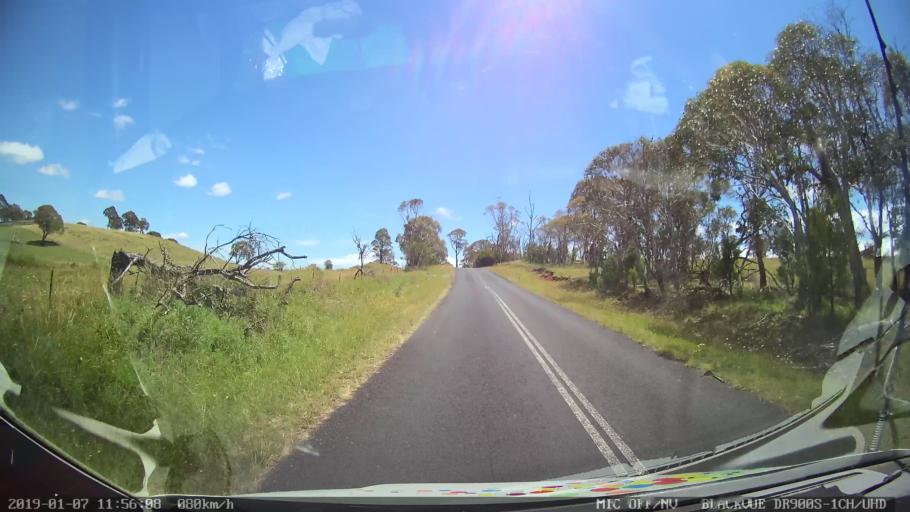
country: AU
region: New South Wales
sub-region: Guyra
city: Guyra
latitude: -30.2779
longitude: 151.6739
